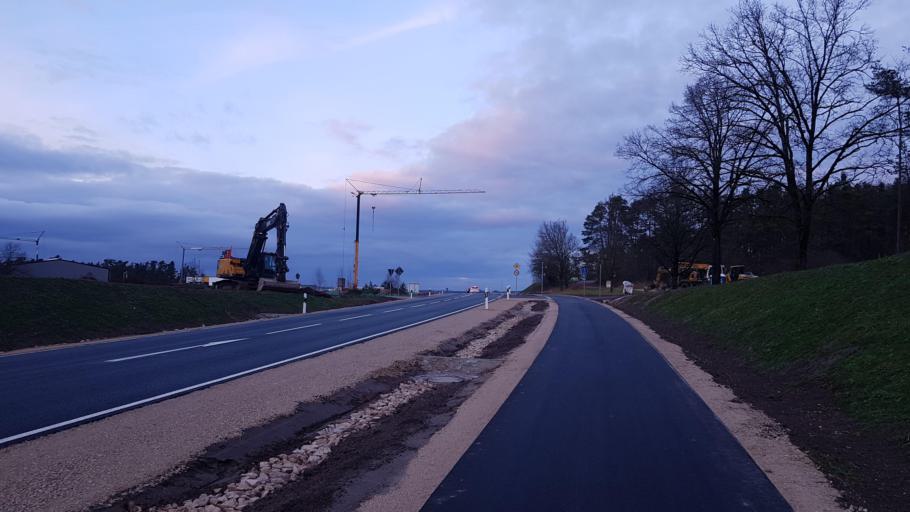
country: DE
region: Bavaria
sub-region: Regierungsbezirk Mittelfranken
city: Hilpoltstein
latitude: 49.1752
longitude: 11.1811
